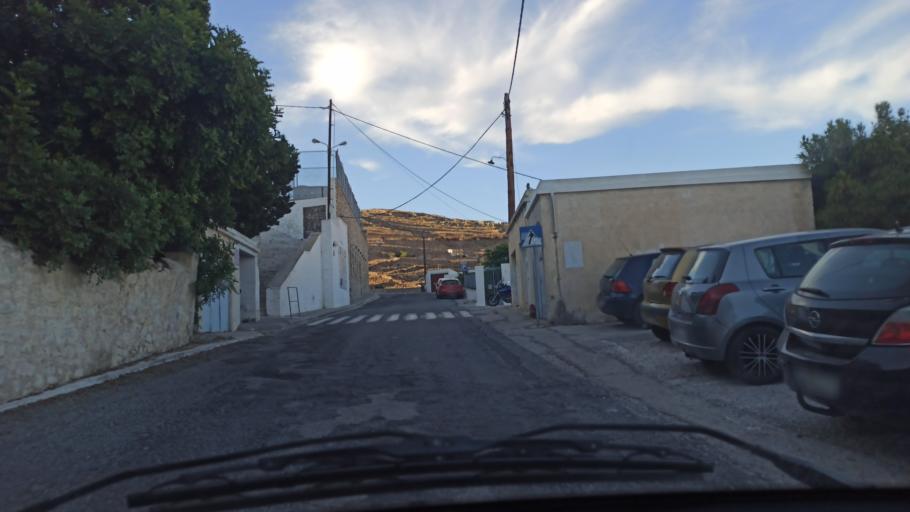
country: GR
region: South Aegean
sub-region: Nomos Kykladon
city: Ano Syros
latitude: 37.4487
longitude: 24.9370
